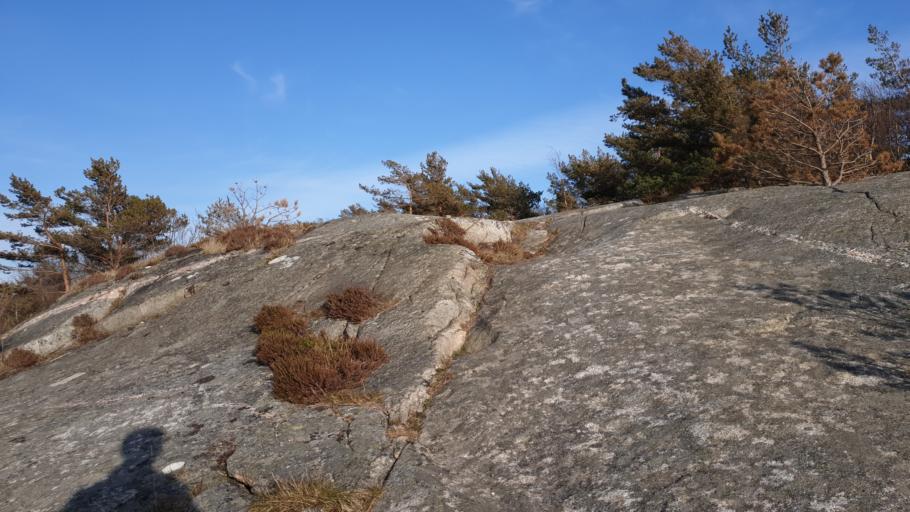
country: SE
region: Vaestra Goetaland
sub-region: Goteborg
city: Billdal
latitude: 57.5946
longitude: 11.9069
